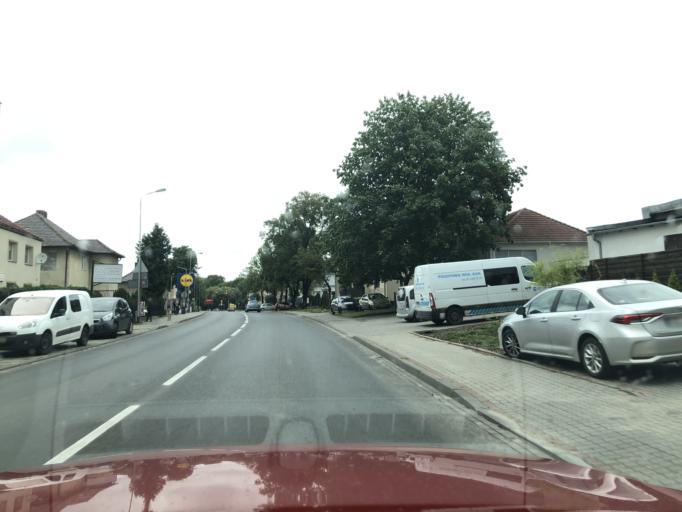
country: PL
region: Greater Poland Voivodeship
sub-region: Powiat szamotulski
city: Wronki
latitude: 52.7082
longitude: 16.3792
